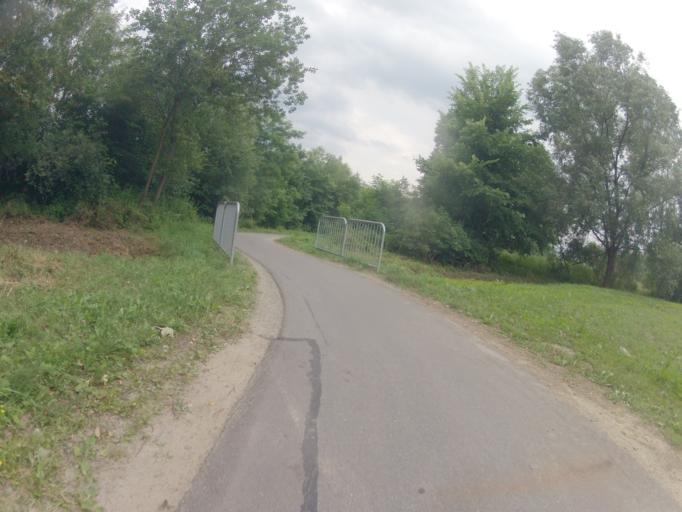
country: PL
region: Lesser Poland Voivodeship
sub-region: Powiat nowosadecki
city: Stary Sacz
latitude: 49.5402
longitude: 20.6570
